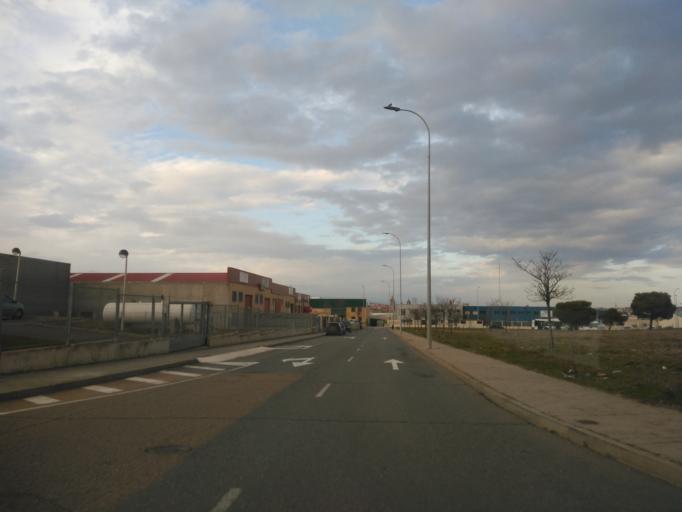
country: ES
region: Castille and Leon
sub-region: Provincia de Salamanca
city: Carbajosa de la Sagrada
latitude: 40.9375
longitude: -5.6638
